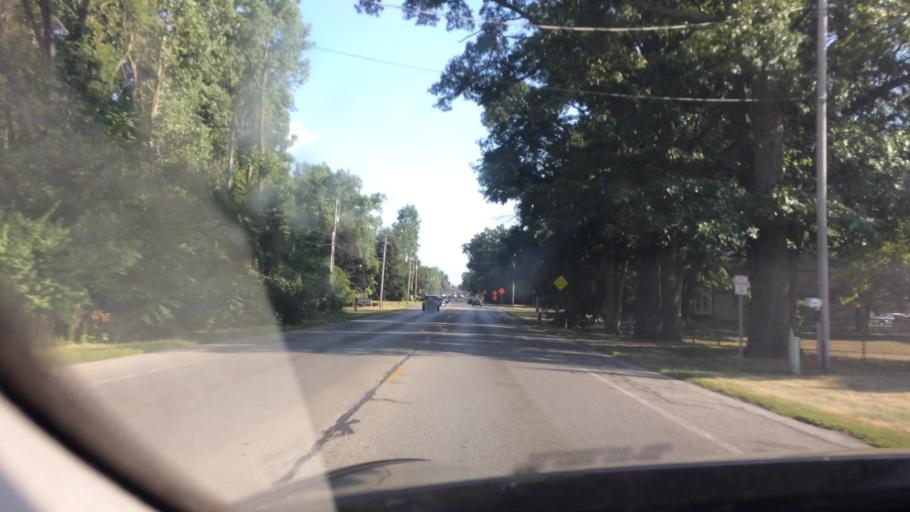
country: US
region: Ohio
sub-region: Lucas County
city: Holland
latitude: 41.6436
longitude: -83.7036
